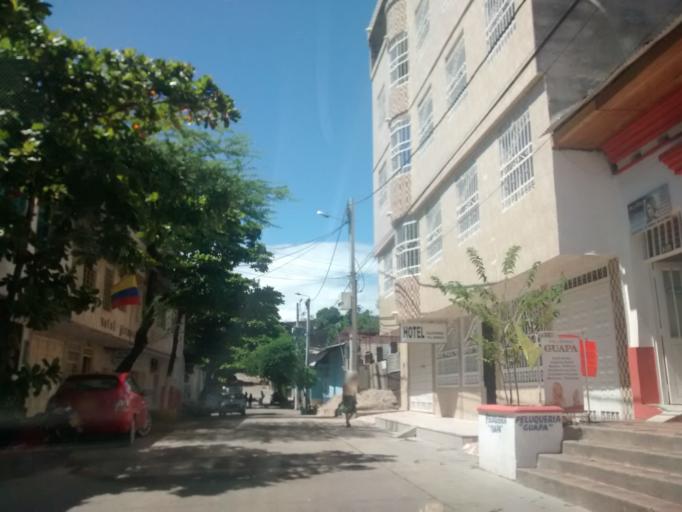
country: CO
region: Cundinamarca
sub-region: Girardot
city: Girardot City
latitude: 4.2953
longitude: -74.8050
